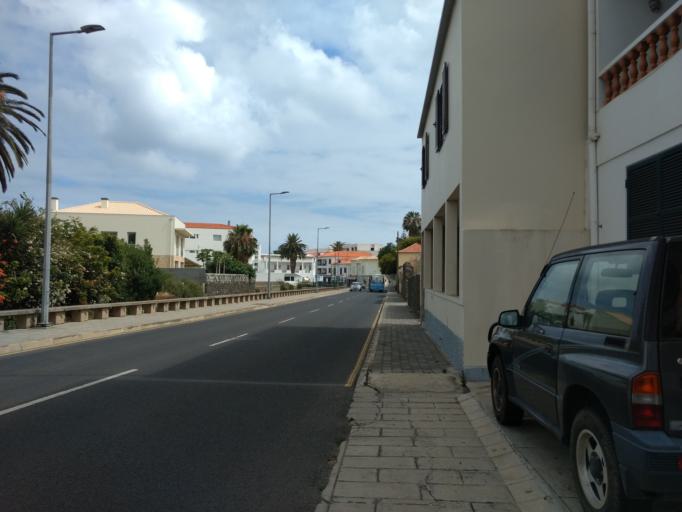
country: PT
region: Madeira
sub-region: Porto Santo
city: Vila de Porto Santo
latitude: 33.0619
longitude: -16.3350
